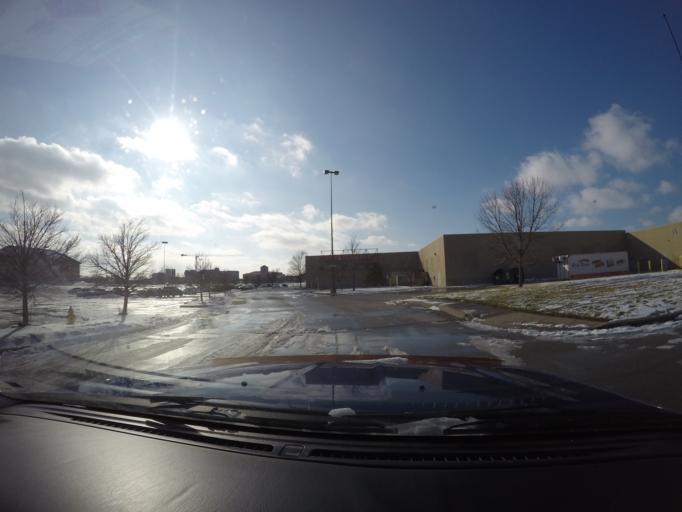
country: US
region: Kansas
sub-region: Johnson County
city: Olathe
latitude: 38.8573
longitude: -94.8196
